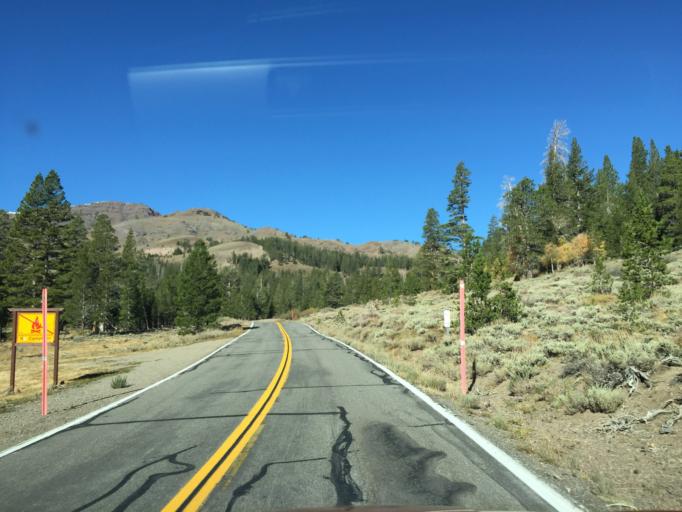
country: US
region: California
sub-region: Mono County
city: Bridgeport
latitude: 38.3145
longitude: -119.6053
